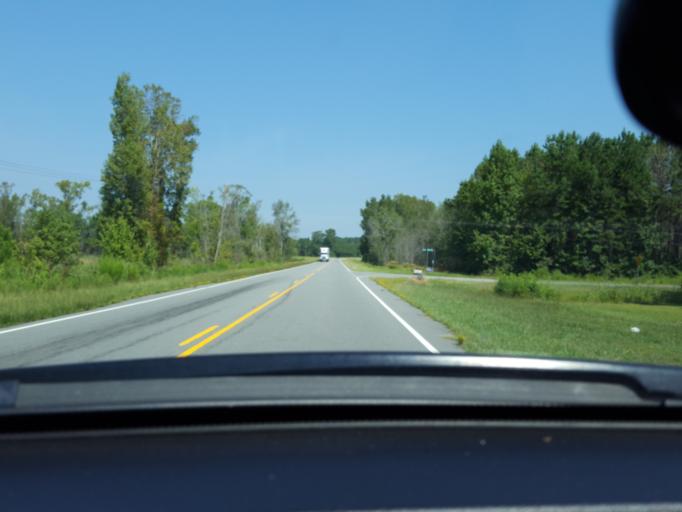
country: US
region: North Carolina
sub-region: Bladen County
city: Elizabethtown
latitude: 34.6762
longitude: -78.4900
